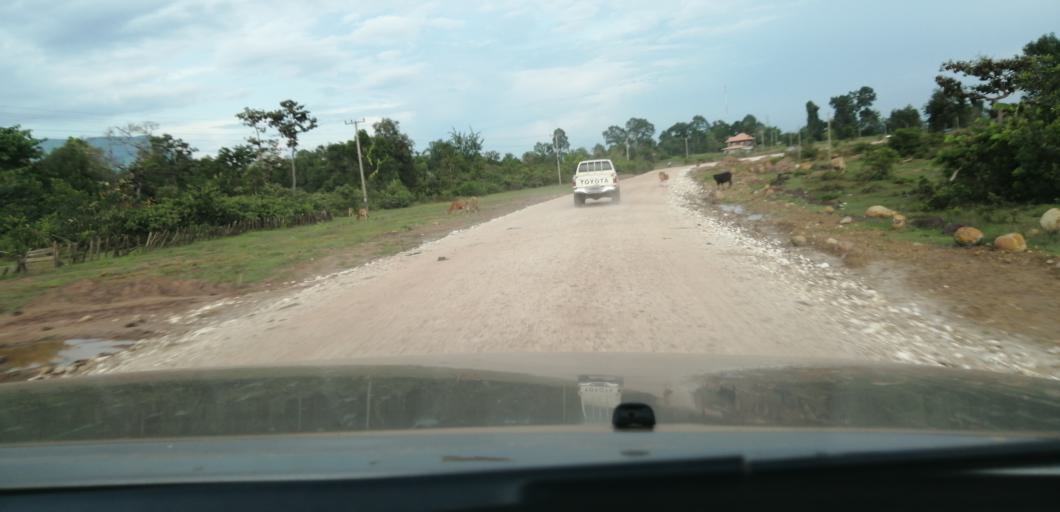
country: LA
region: Attapu
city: Attapu
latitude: 14.7098
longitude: 106.4899
